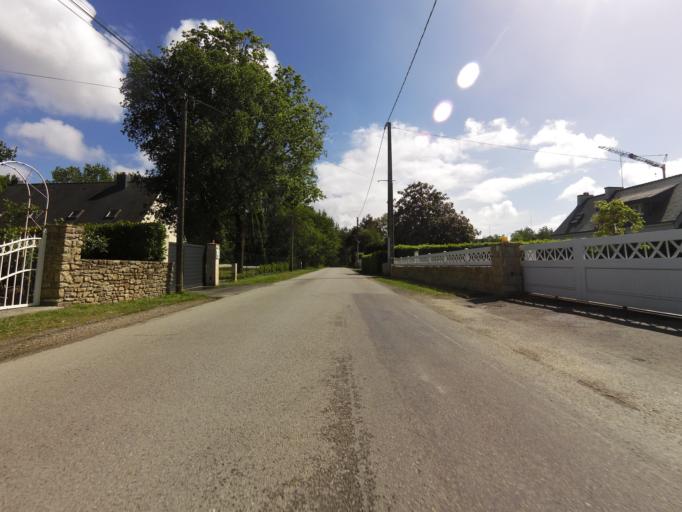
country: FR
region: Brittany
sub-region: Departement du Morbihan
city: Plougoumelen
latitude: 47.6610
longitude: -2.9028
